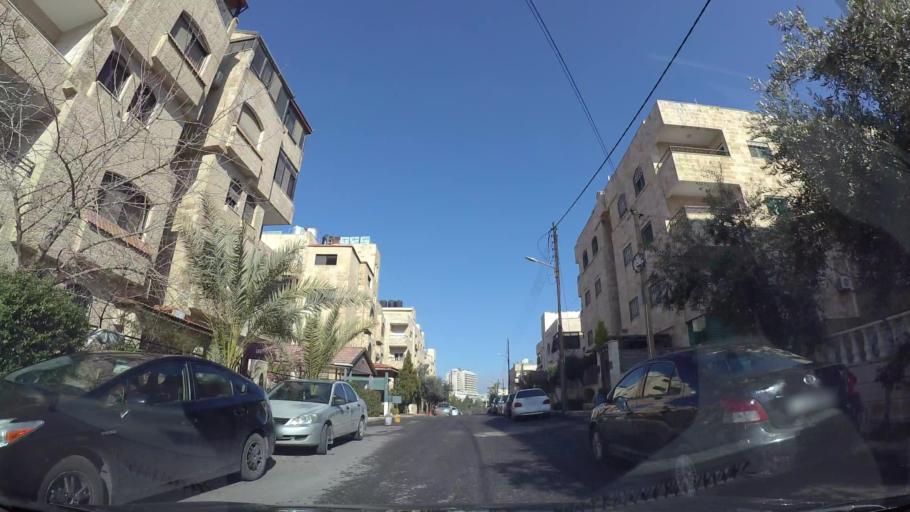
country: JO
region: Amman
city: Al Jubayhah
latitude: 32.0023
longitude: 35.8786
